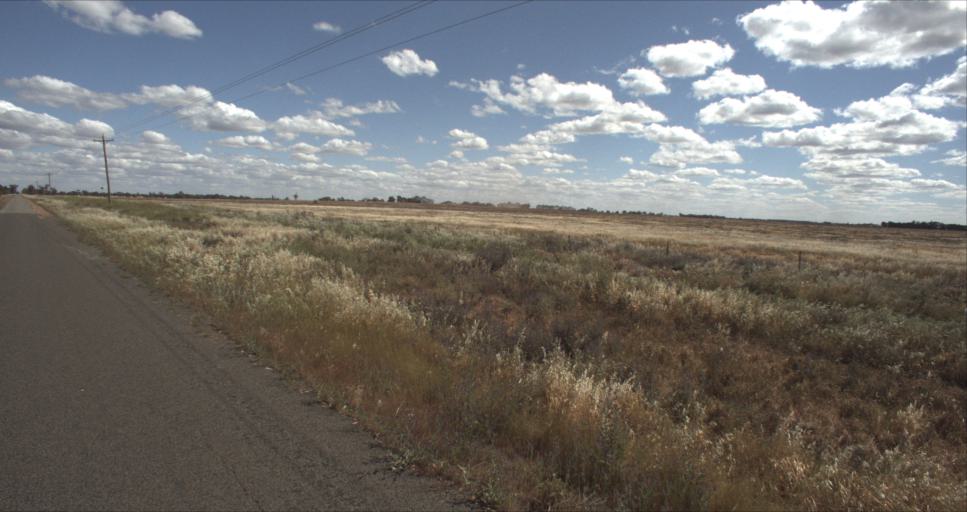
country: AU
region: New South Wales
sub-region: Leeton
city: Leeton
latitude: -34.4731
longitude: 146.2505
